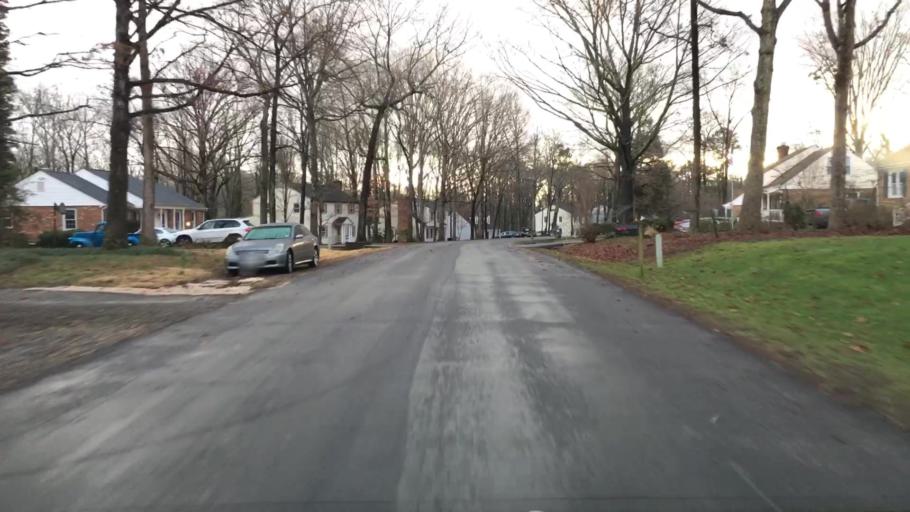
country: US
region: Virginia
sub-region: Chesterfield County
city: Bon Air
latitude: 37.5183
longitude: -77.6233
